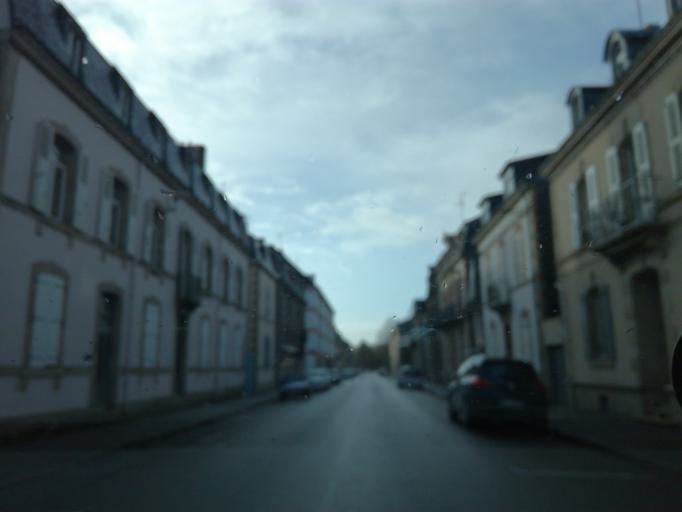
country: FR
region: Brittany
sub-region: Departement du Morbihan
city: Pontivy
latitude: 48.0618
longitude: -2.9672
